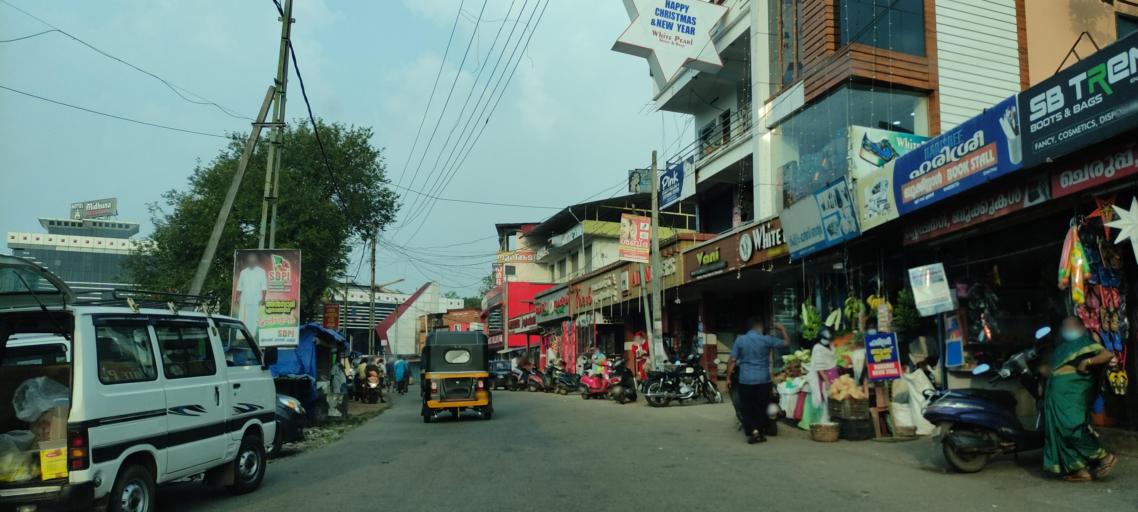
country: IN
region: Kerala
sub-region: Pattanamtitta
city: Adur
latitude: 9.0899
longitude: 76.7547
